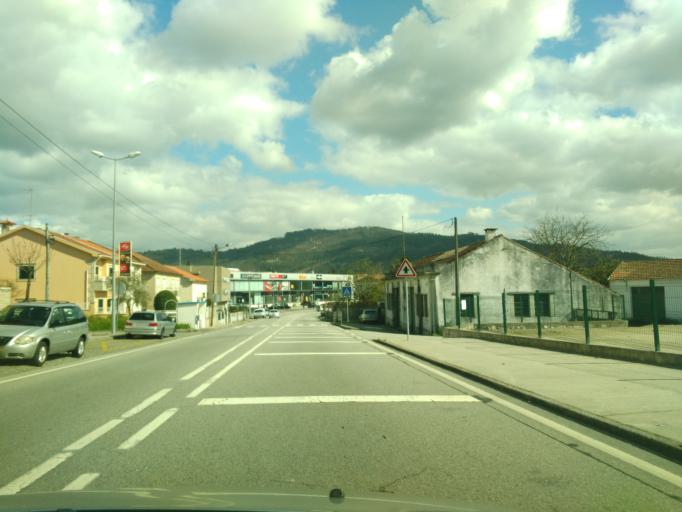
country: PT
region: Braga
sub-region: Braga
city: Braga
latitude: 41.5346
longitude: -8.4212
